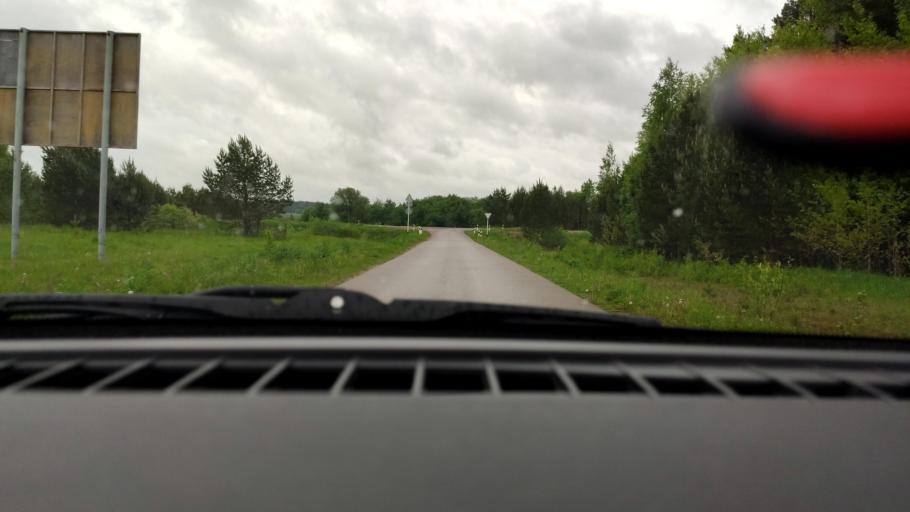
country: RU
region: Perm
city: Karagay
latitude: 58.2526
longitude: 54.8700
